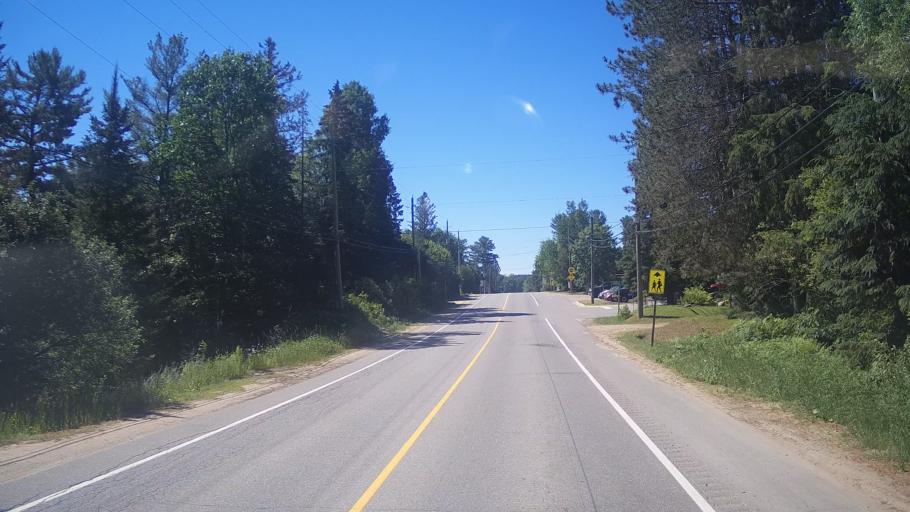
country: CA
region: Ontario
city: Huntsville
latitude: 45.3472
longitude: -79.2014
